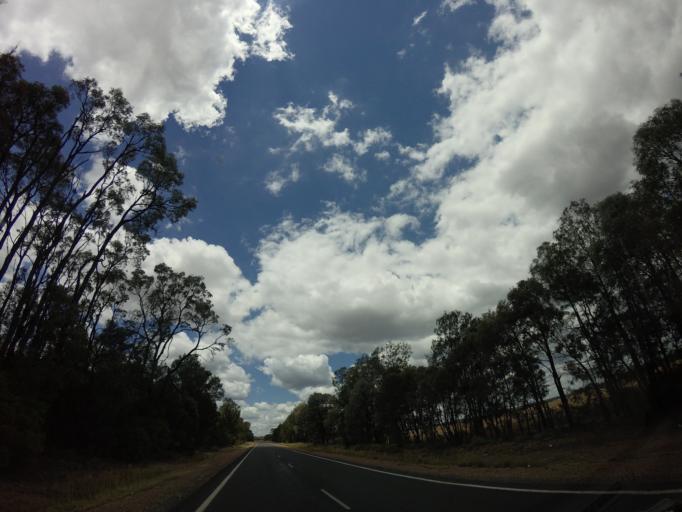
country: AU
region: Queensland
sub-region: Goondiwindi
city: Goondiwindi
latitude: -28.0068
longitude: 150.8850
